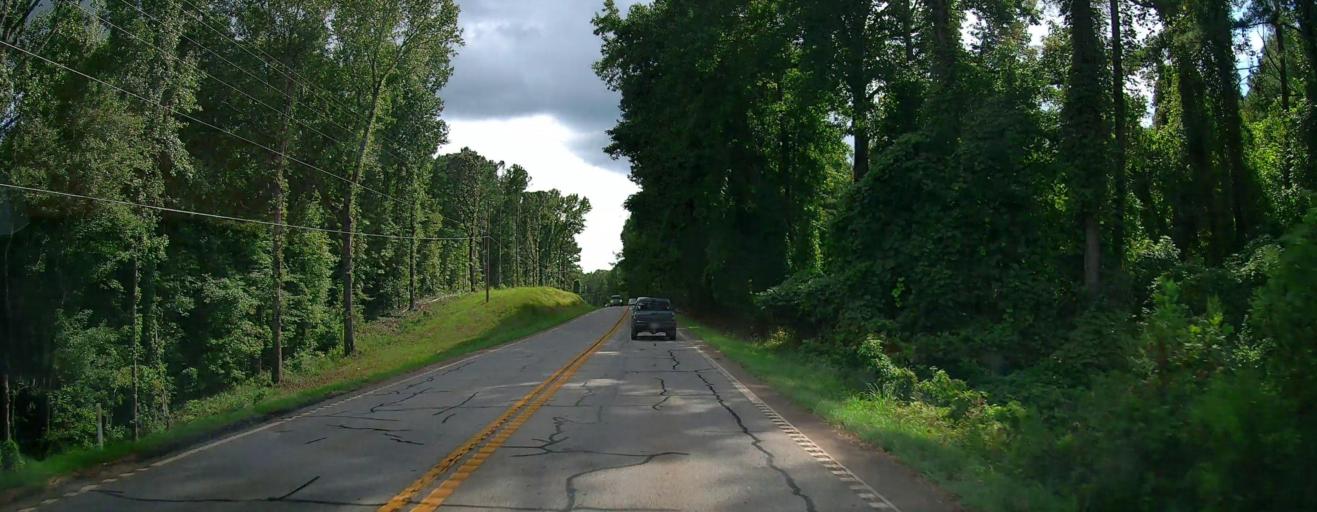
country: US
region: Georgia
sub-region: Harris County
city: Hamilton
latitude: 32.7334
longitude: -84.8733
